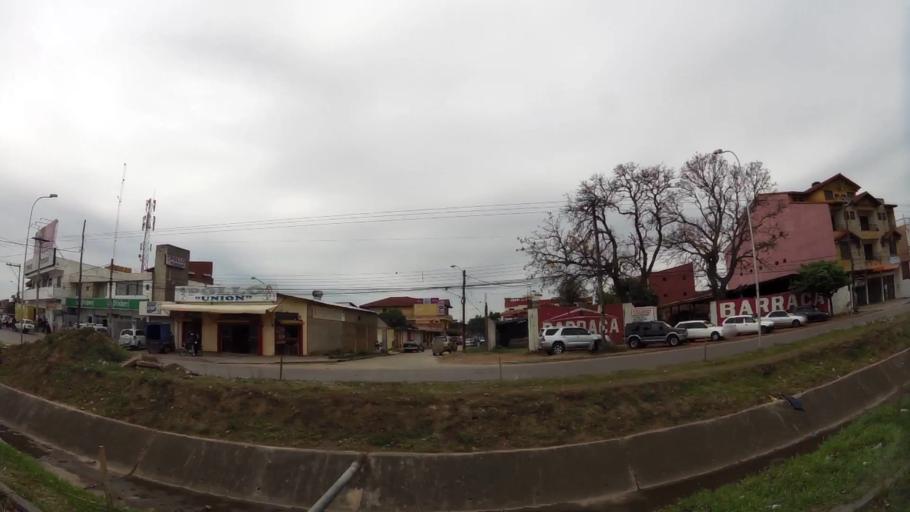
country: BO
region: Santa Cruz
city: Santa Cruz de la Sierra
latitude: -17.8330
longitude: -63.1867
